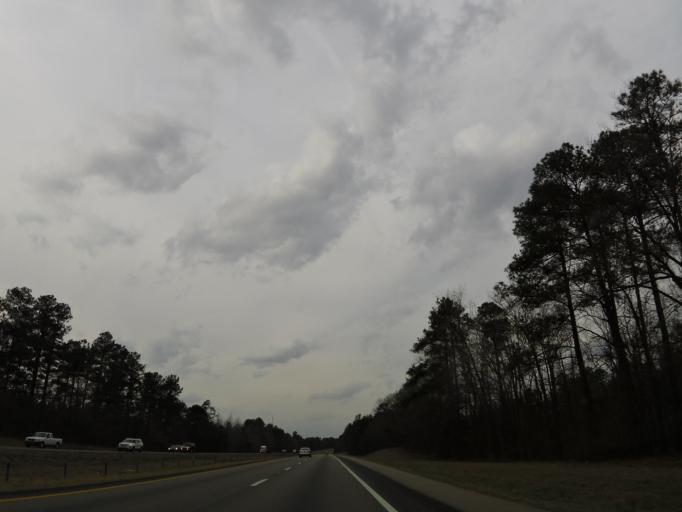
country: US
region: South Carolina
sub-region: Calhoun County
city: Oak Grove
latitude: 33.6852
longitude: -80.9064
